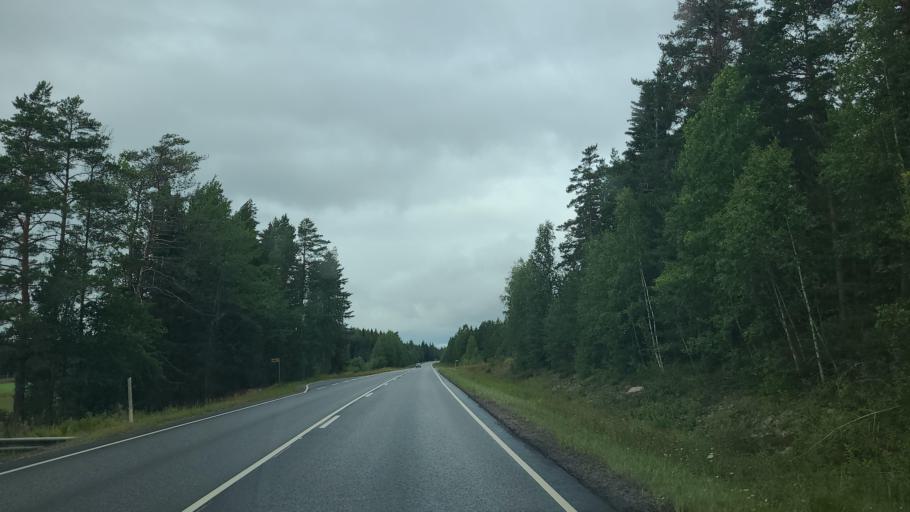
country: FI
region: Varsinais-Suomi
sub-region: Aboland-Turunmaa
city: Kimito
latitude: 60.2051
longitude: 22.6476
